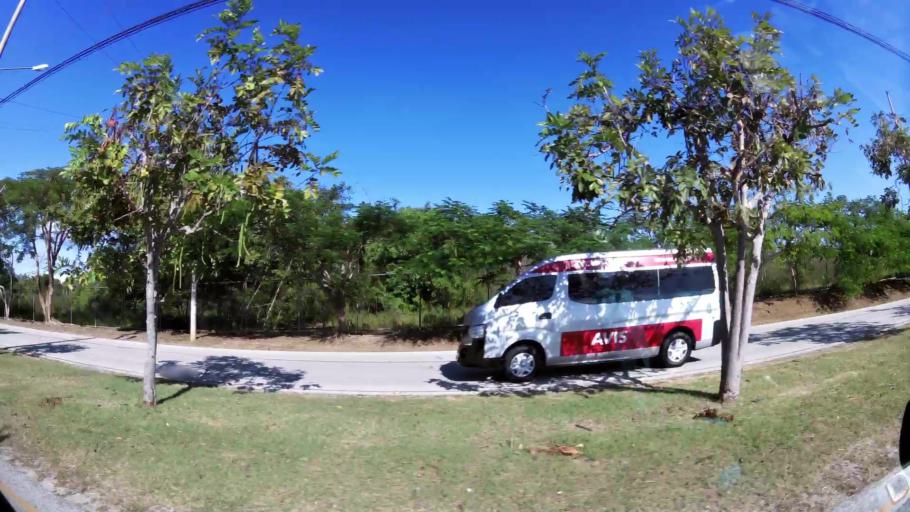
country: CR
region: Guanacaste
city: Liberia
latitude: 10.6007
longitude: -85.5297
